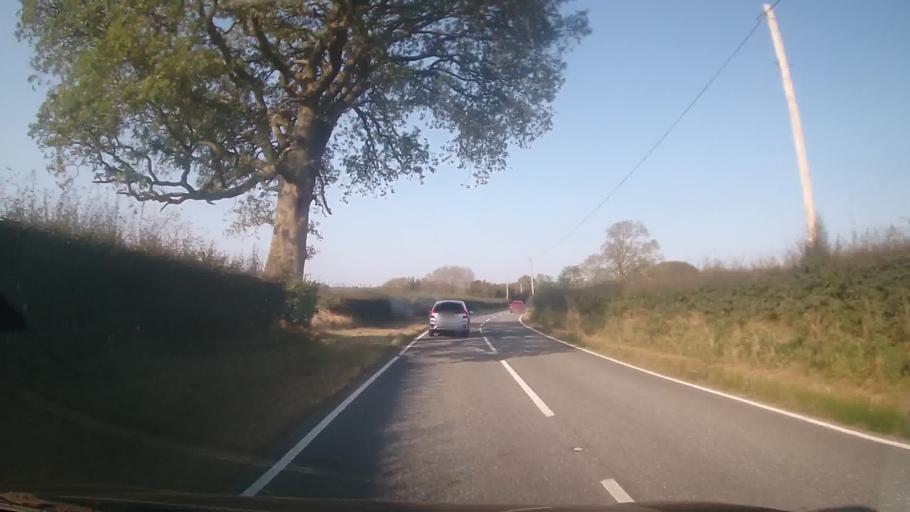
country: GB
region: Wales
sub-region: County of Ceredigion
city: Lledrod
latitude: 52.2678
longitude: -3.8790
